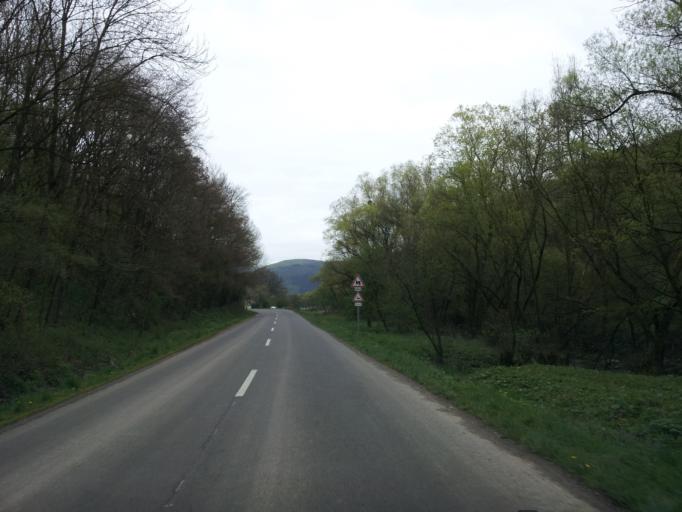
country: HU
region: Borsod-Abauj-Zemplen
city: Szendro
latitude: 48.4979
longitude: 20.6750
